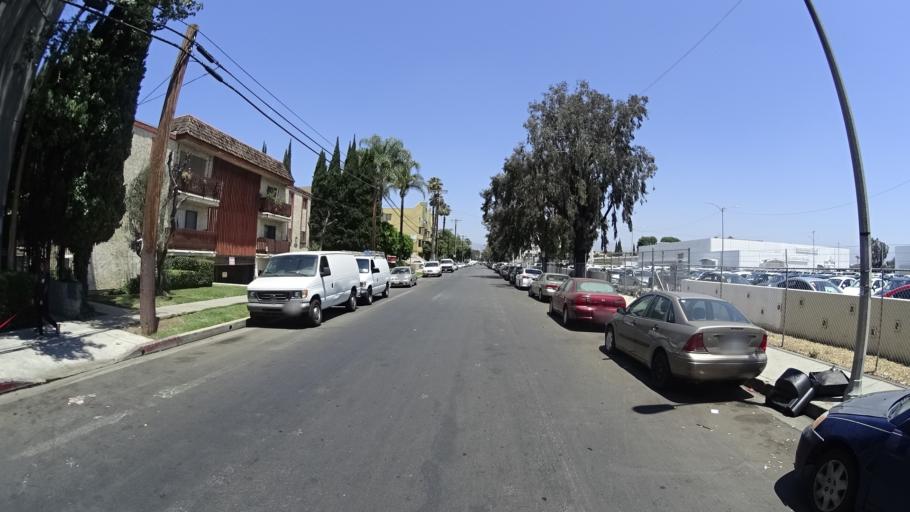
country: US
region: California
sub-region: Los Angeles County
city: Van Nuys
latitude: 34.2220
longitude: -118.4536
